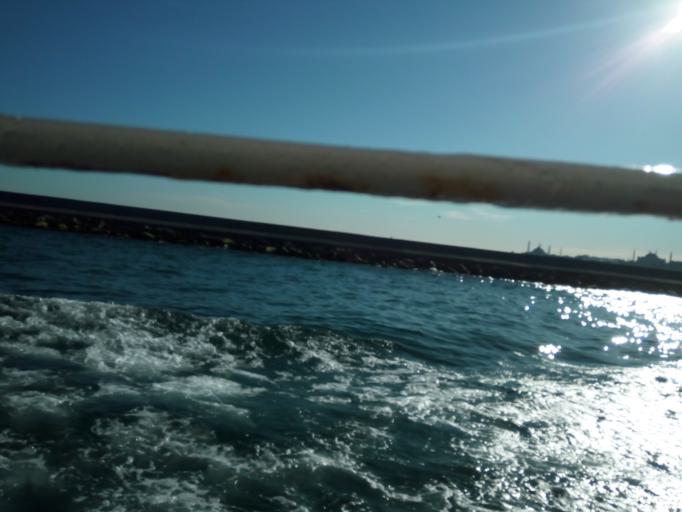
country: TR
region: Istanbul
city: UEskuedar
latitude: 41.0061
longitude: 29.0048
